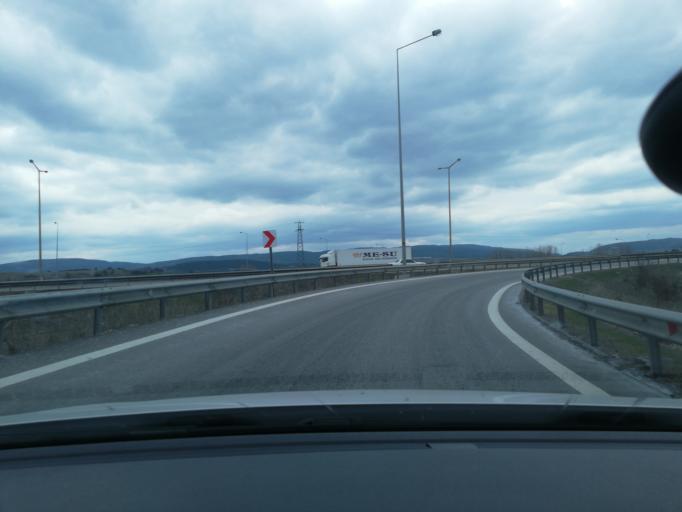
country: TR
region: Bolu
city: Yenicaga
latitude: 40.7628
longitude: 32.0086
